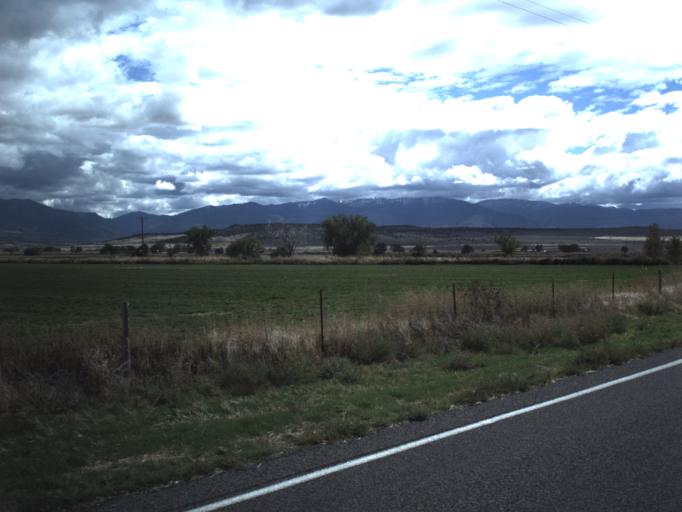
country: US
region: Utah
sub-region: Millard County
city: Fillmore
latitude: 39.0496
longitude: -112.4098
